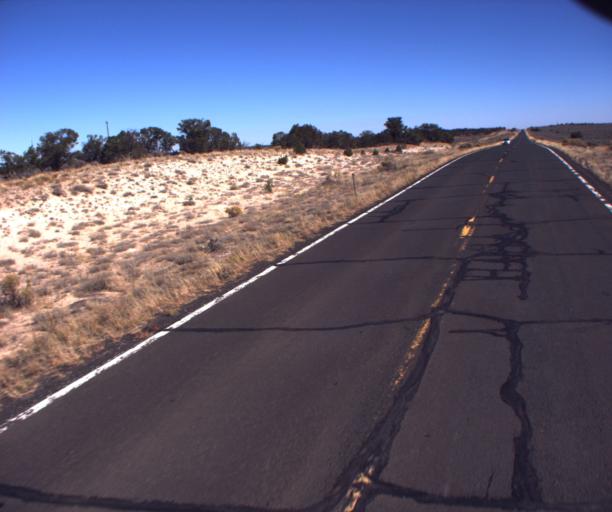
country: US
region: Arizona
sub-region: Navajo County
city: First Mesa
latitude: 35.7355
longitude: -110.0911
